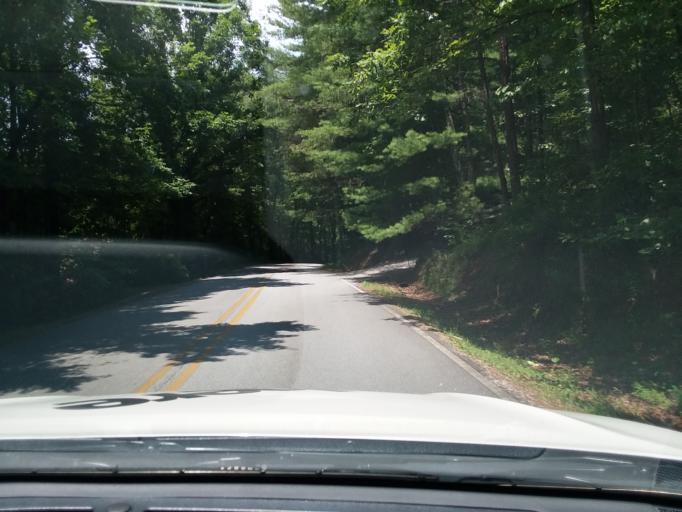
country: US
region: Georgia
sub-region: Rabun County
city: Clayton
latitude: 34.8207
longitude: -83.4255
